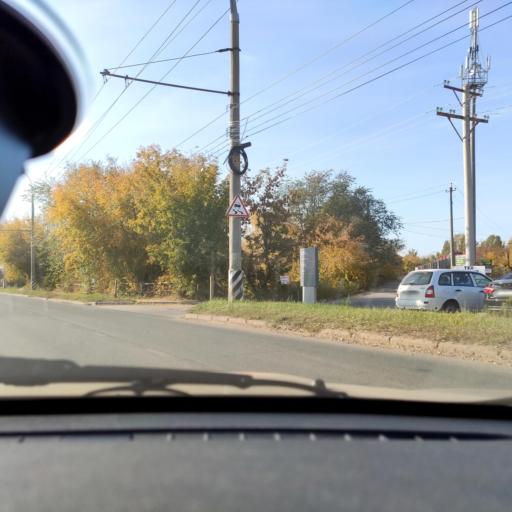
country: RU
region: Samara
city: Tol'yatti
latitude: 53.5455
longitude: 49.3014
